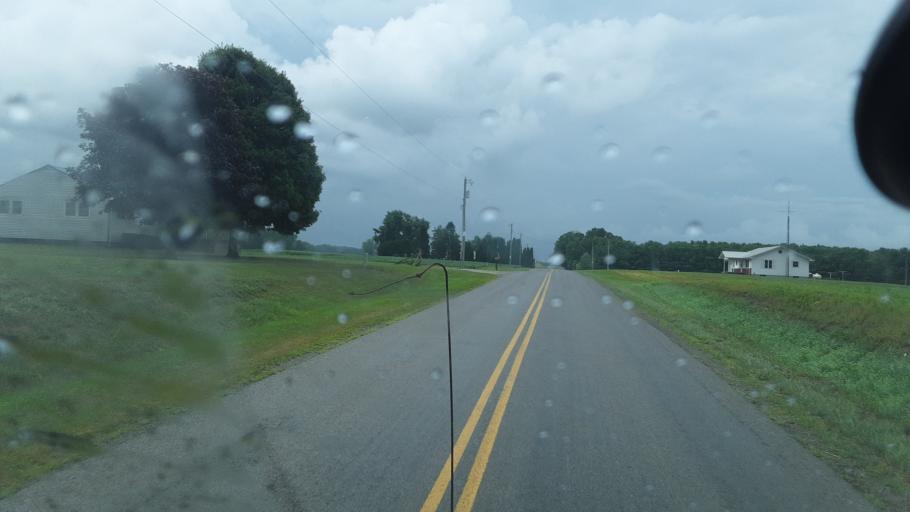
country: US
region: Indiana
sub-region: Steuben County
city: Fremont
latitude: 41.6552
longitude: -84.7950
